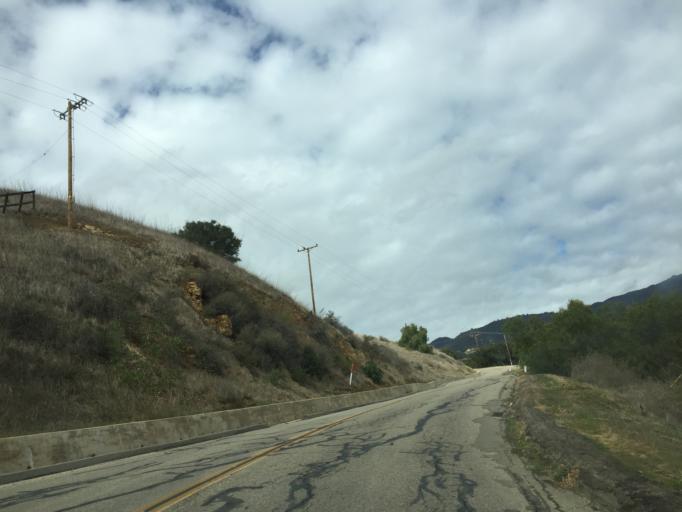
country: US
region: California
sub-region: Santa Barbara County
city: Goleta
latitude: 34.4608
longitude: -119.7963
